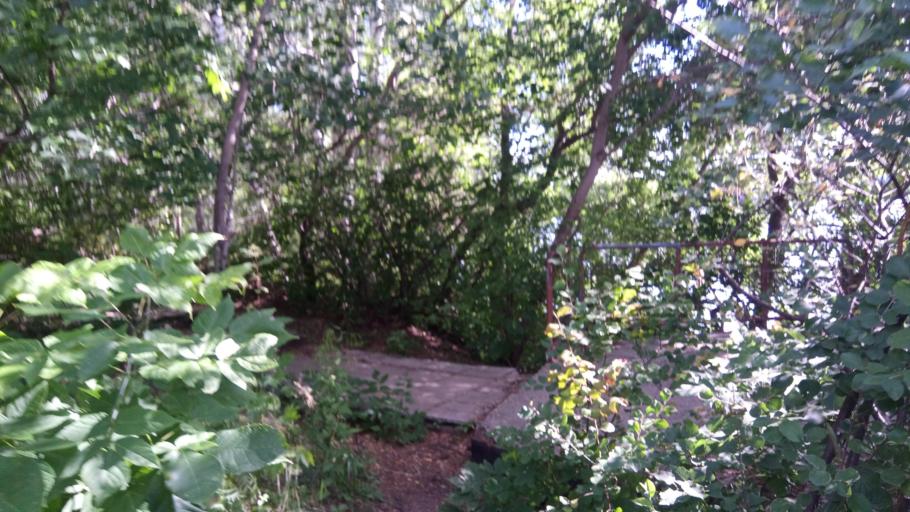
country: RU
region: Chelyabinsk
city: Chebarkul'
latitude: 55.0193
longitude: 60.3101
